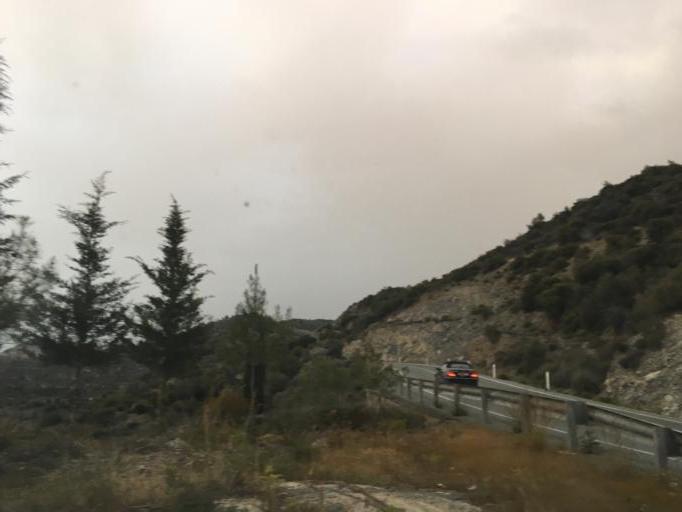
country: CY
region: Limassol
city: Parekklisha
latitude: 34.7963
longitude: 33.1522
